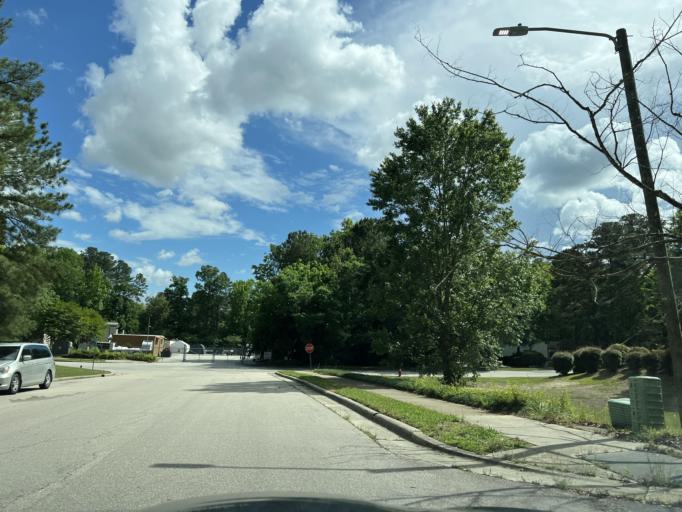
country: US
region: North Carolina
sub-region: Wake County
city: Wake Forest
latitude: 35.8941
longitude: -78.5688
